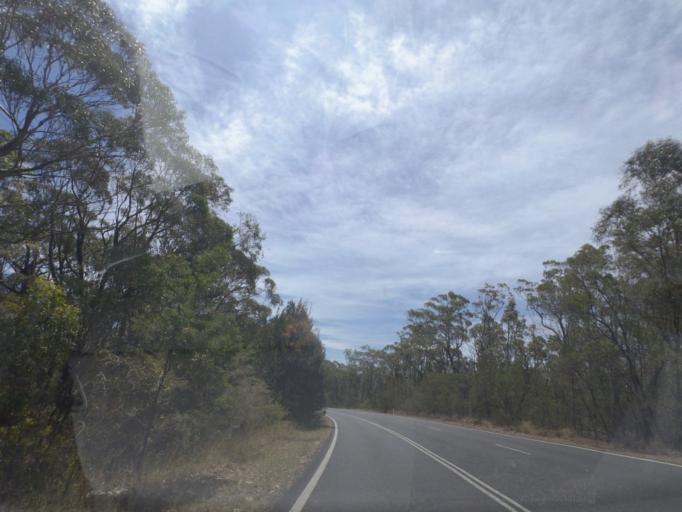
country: AU
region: New South Wales
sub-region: Wingecarribee
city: Colo Vale
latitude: -34.3951
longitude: 150.5331
